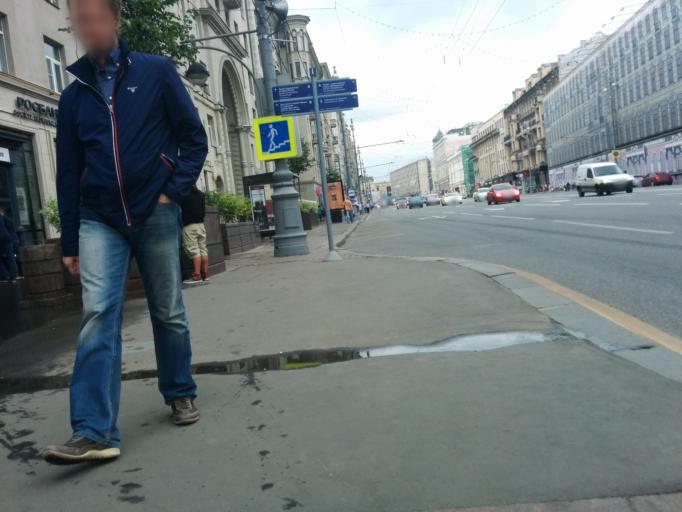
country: RU
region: Moscow
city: Moscow
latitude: 55.7620
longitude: 37.6092
